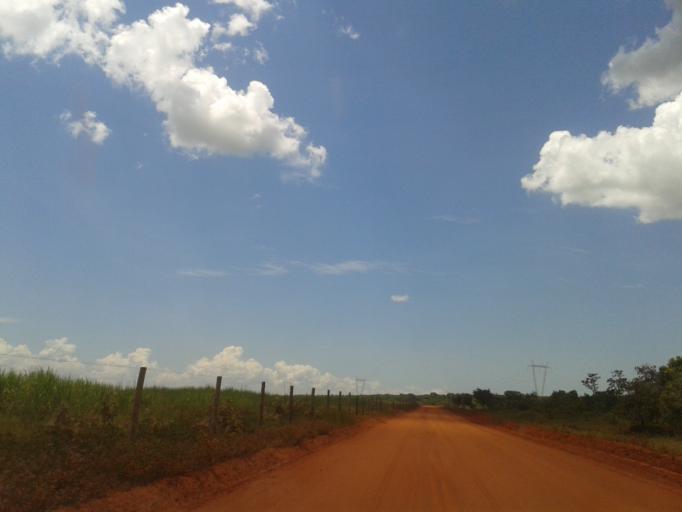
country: BR
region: Minas Gerais
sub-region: Santa Vitoria
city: Santa Vitoria
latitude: -19.1693
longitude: -50.4073
